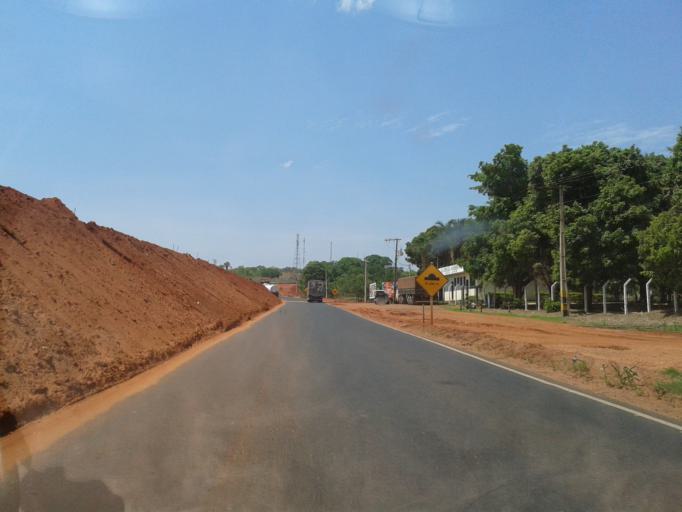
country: BR
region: Minas Gerais
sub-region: Monte Alegre De Minas
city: Monte Alegre de Minas
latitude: -18.8650
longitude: -48.8664
